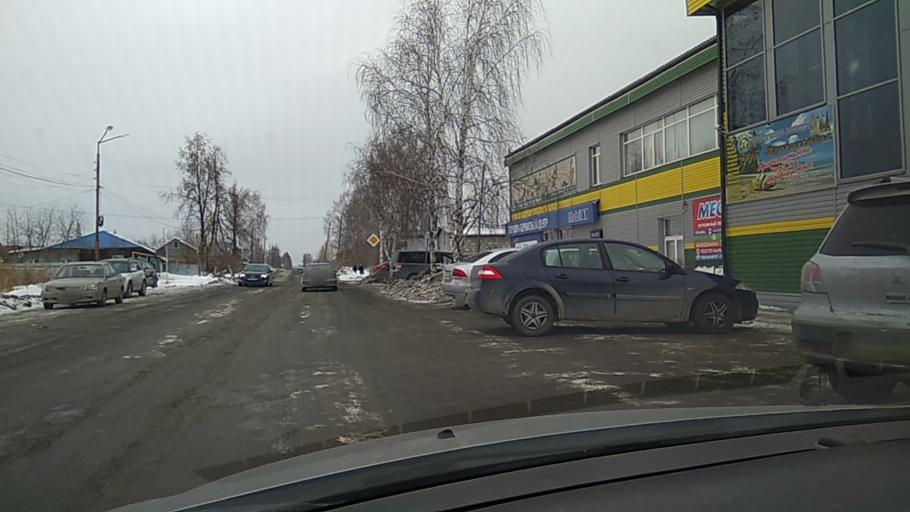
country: RU
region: Sverdlovsk
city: Revda
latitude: 56.8060
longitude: 59.9356
